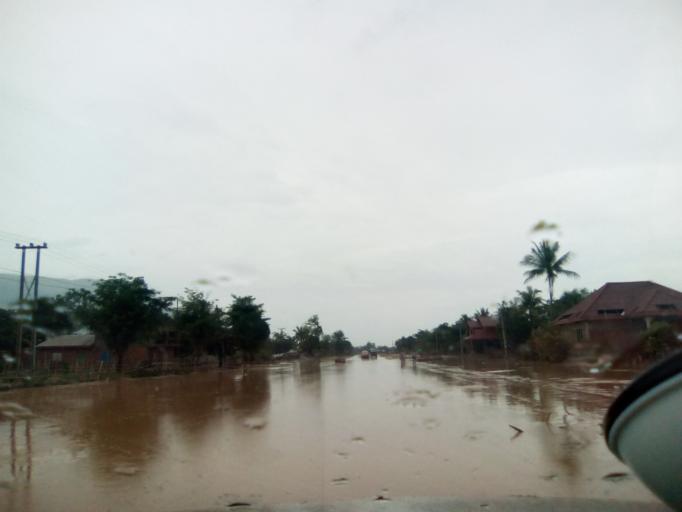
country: LA
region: Attapu
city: Attapu
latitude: 14.7036
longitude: 106.5232
